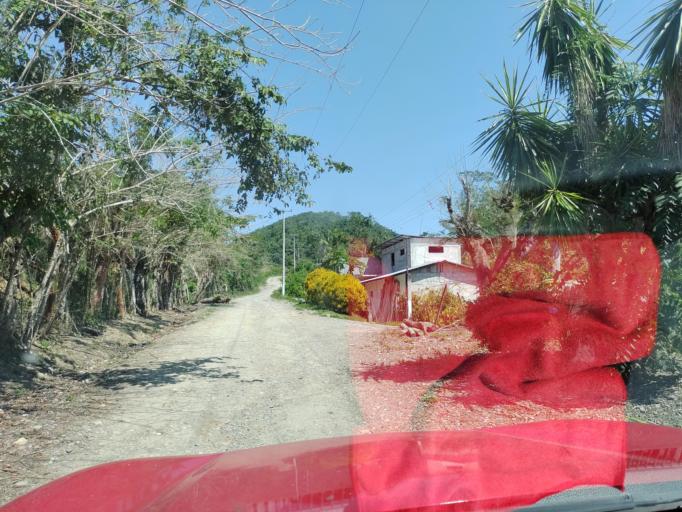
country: MX
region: Veracruz
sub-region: Papantla
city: Polutla
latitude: 20.5026
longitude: -97.2138
